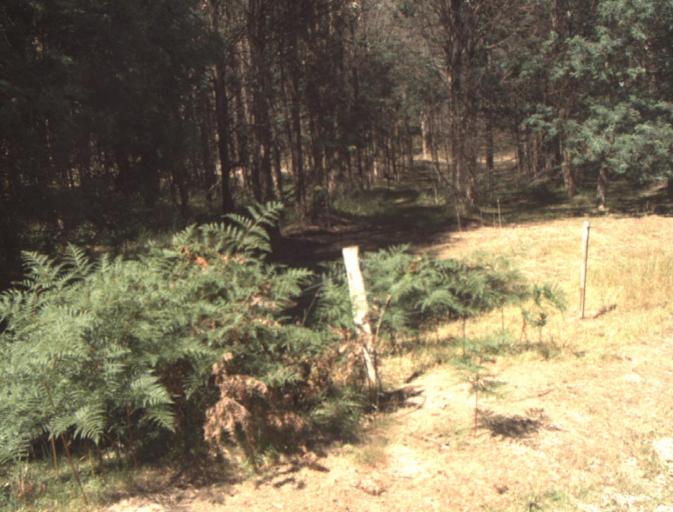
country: AU
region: Tasmania
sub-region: Dorset
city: Scottsdale
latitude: -41.2725
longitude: 147.3483
